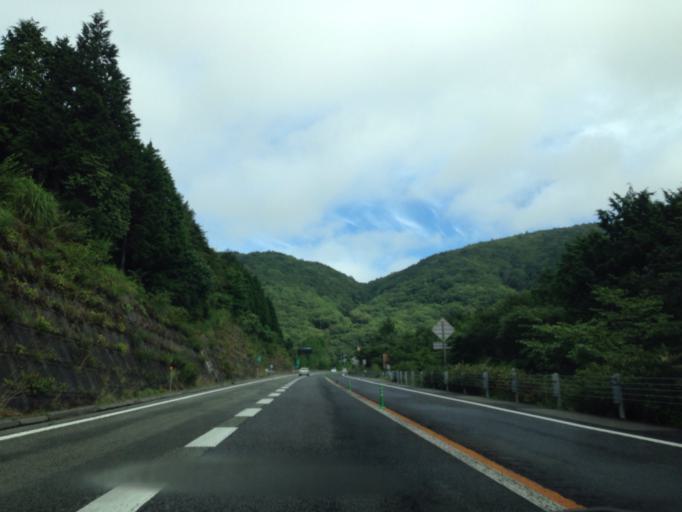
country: JP
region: Shizuoka
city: Gotemba
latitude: 35.3761
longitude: 138.8468
